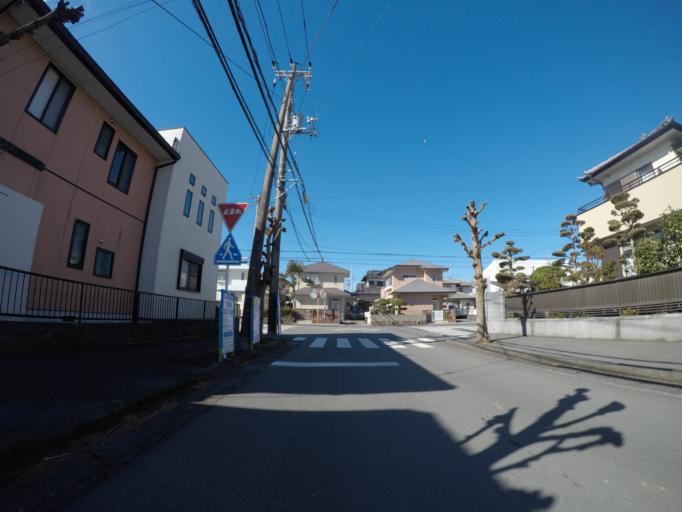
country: JP
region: Shizuoka
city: Numazu
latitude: 35.1355
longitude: 138.8030
